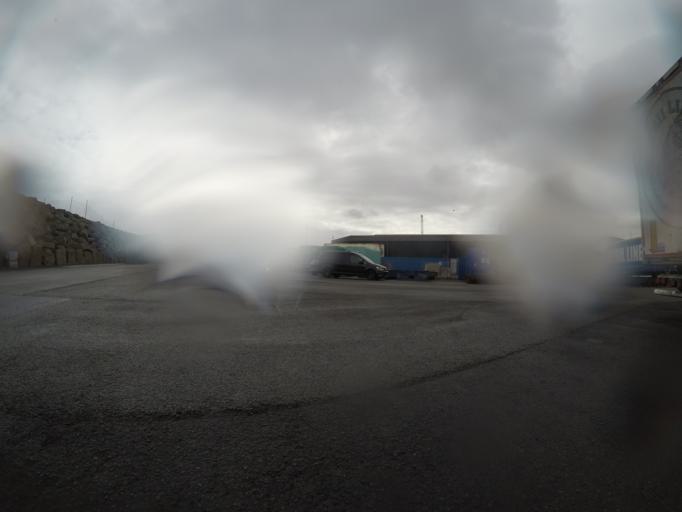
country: FO
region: Streymoy
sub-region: Torshavn
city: Torshavn
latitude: 62.0064
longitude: -6.7631
